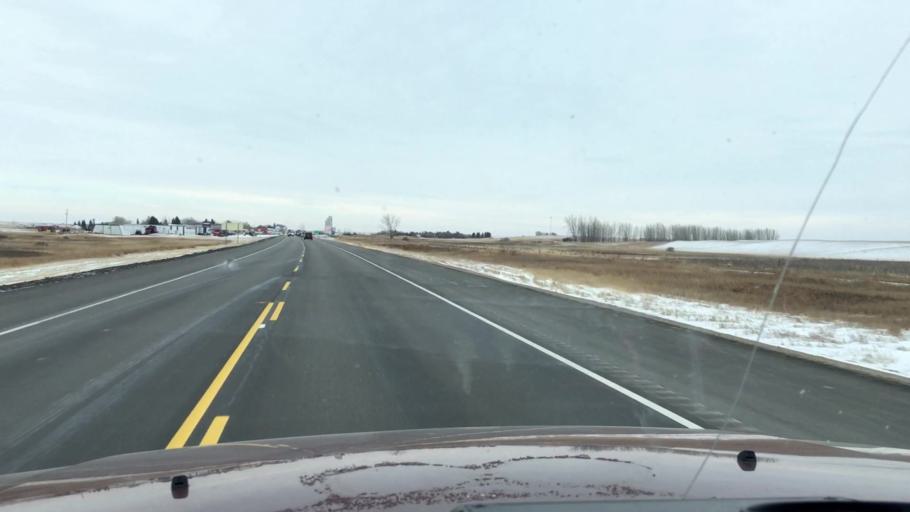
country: CA
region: Saskatchewan
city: Moose Jaw
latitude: 50.8578
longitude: -105.5817
